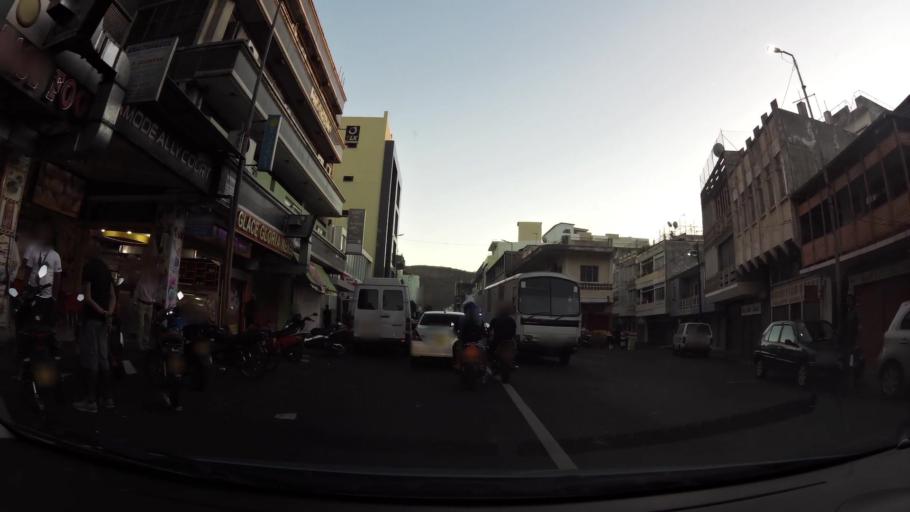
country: MU
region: Port Louis
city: Port Louis
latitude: -20.1600
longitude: 57.5091
